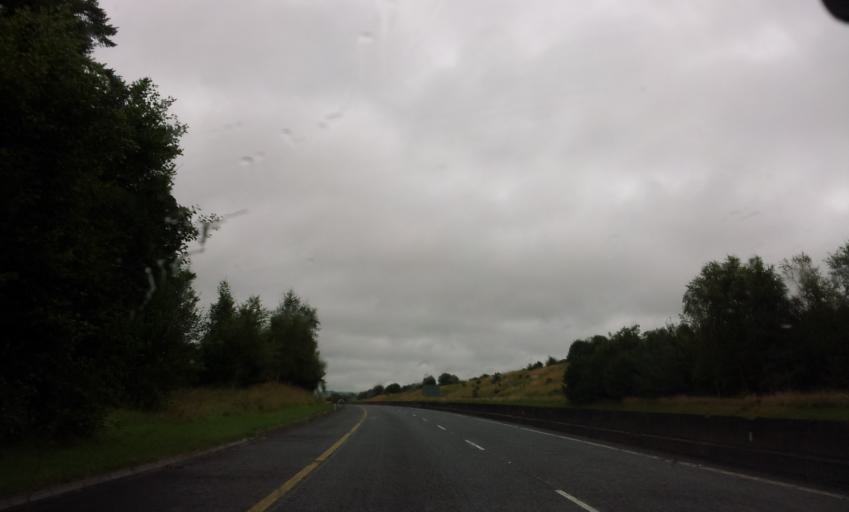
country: IE
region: Munster
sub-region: County Cork
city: Fermoy
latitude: 52.1234
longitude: -8.2652
